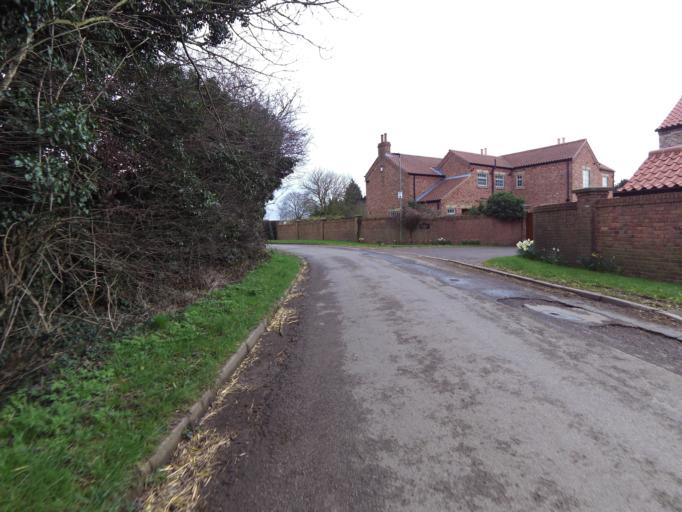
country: GB
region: England
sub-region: Doncaster
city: Moss
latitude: 53.6060
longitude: -1.0705
